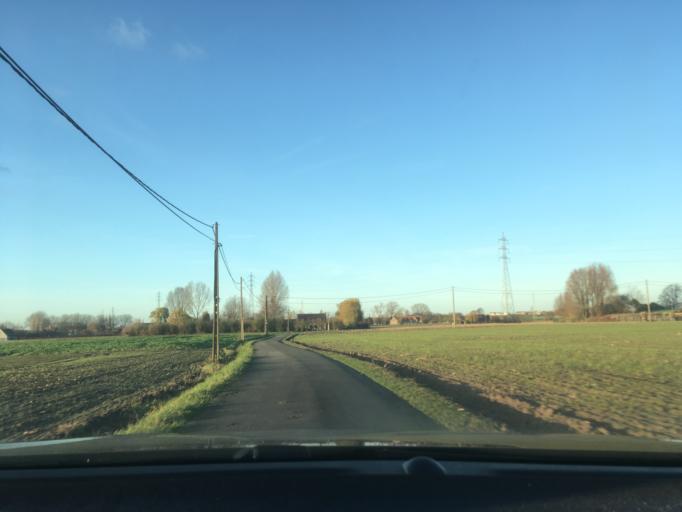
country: BE
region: Flanders
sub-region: Provincie West-Vlaanderen
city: Menen
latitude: 50.8261
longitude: 3.1043
